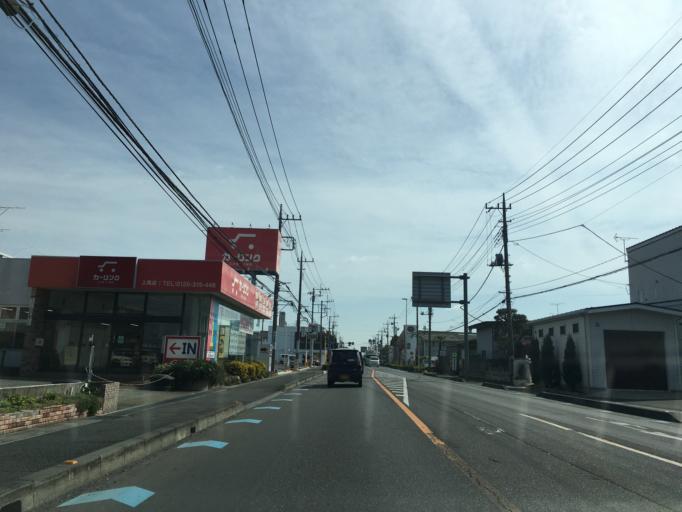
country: JP
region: Saitama
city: Ageoshimo
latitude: 35.9550
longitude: 139.5738
